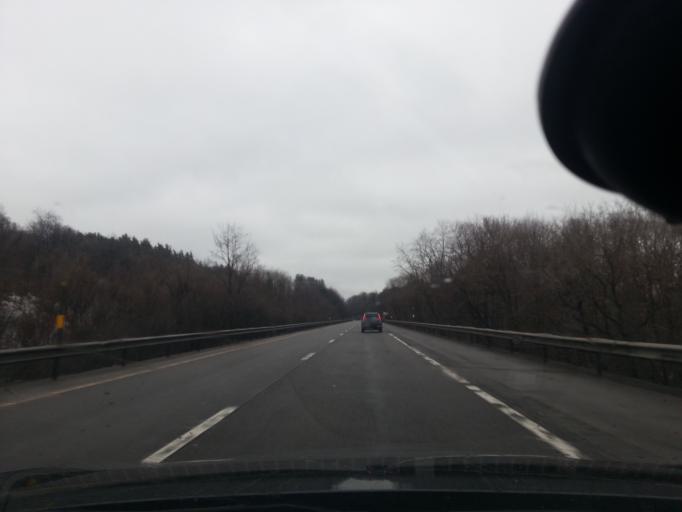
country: US
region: New York
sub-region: Onondaga County
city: Nedrow
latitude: 42.9936
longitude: -76.1349
